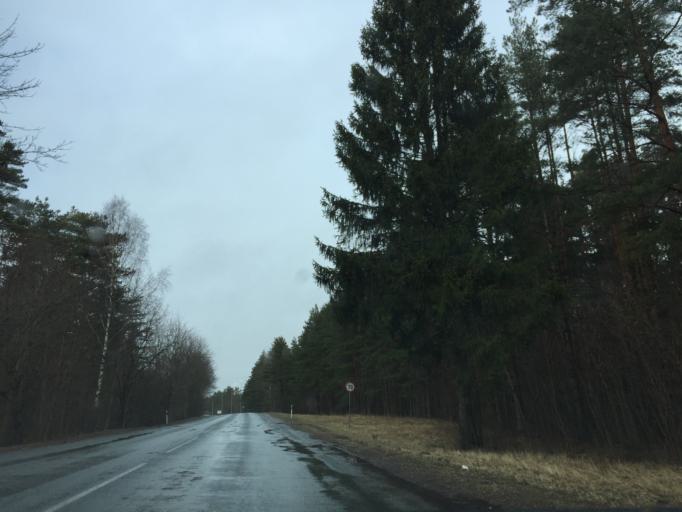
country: EE
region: Laeaene
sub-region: Haapsalu linn
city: Haapsalu
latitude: 58.9174
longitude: 23.5498
